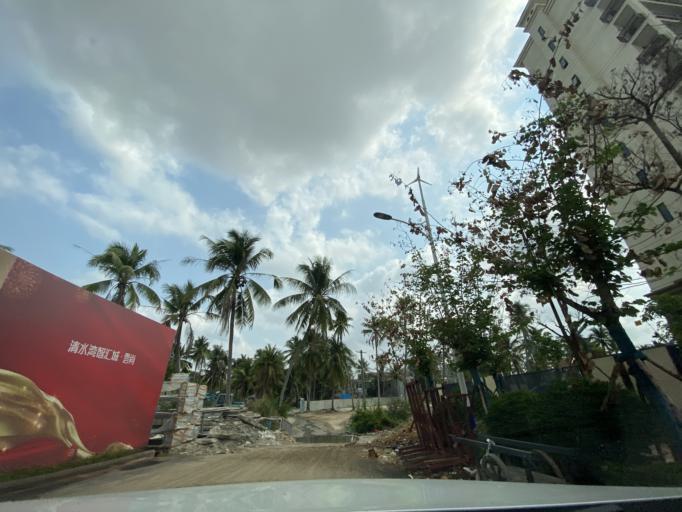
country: CN
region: Hainan
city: Yingzhou
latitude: 18.4095
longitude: 109.8565
